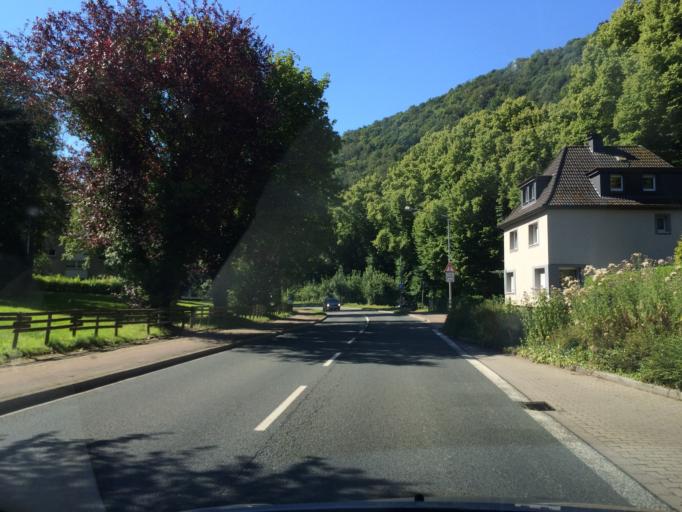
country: DE
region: North Rhine-Westphalia
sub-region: Regierungsbezirk Arnsberg
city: Nachrodt-Wiblingwerde
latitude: 51.3373
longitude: 7.6353
